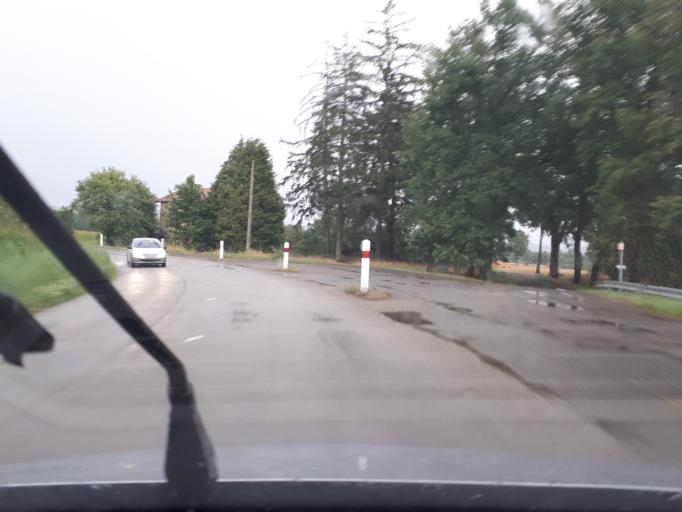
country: FR
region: Rhone-Alpes
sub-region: Departement de la Loire
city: Feurs
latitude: 45.7165
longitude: 4.2607
